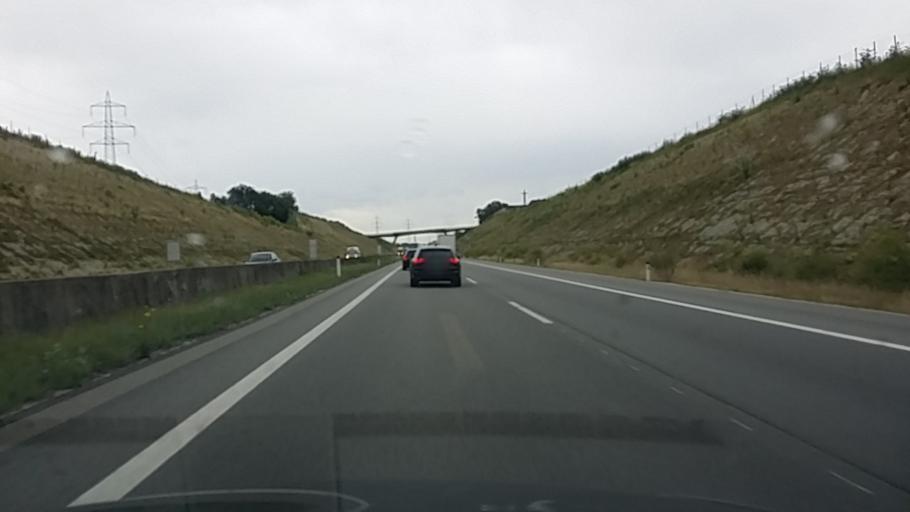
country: AT
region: Upper Austria
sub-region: Politischer Bezirk Ried im Innkreis
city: Ried im Innkreis
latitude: 48.2220
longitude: 13.6131
